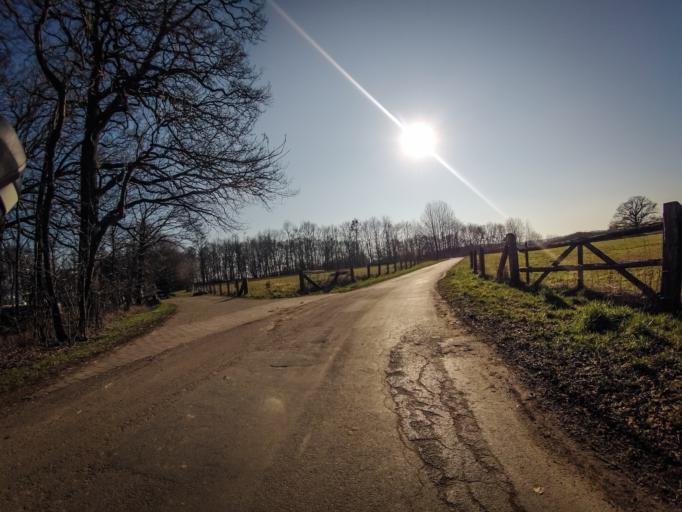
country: DE
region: North Rhine-Westphalia
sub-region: Regierungsbezirk Munster
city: Lotte
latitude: 52.2692
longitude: 7.9396
